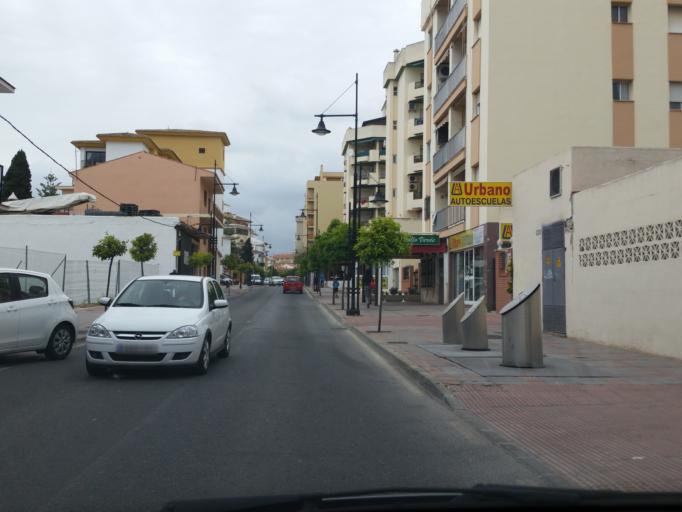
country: ES
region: Andalusia
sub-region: Provincia de Malaga
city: Fuengirola
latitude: 36.5451
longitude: -4.6220
